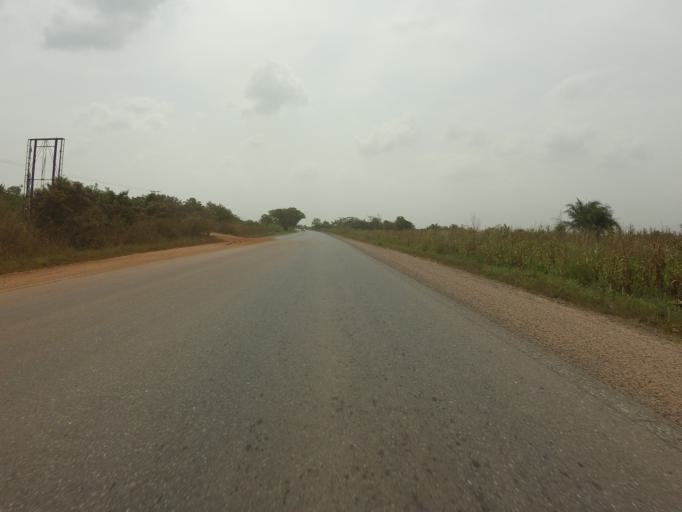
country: GH
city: Akropong
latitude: 6.0576
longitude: 0.0423
